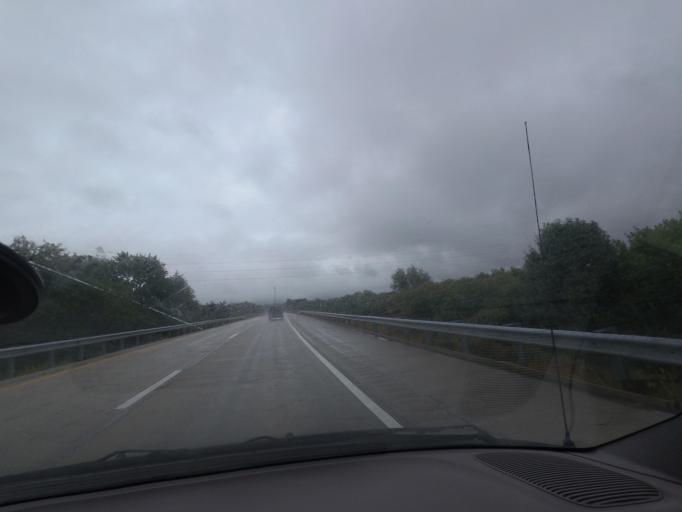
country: US
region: Illinois
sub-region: Champaign County
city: Champaign
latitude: 40.1187
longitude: -88.2884
